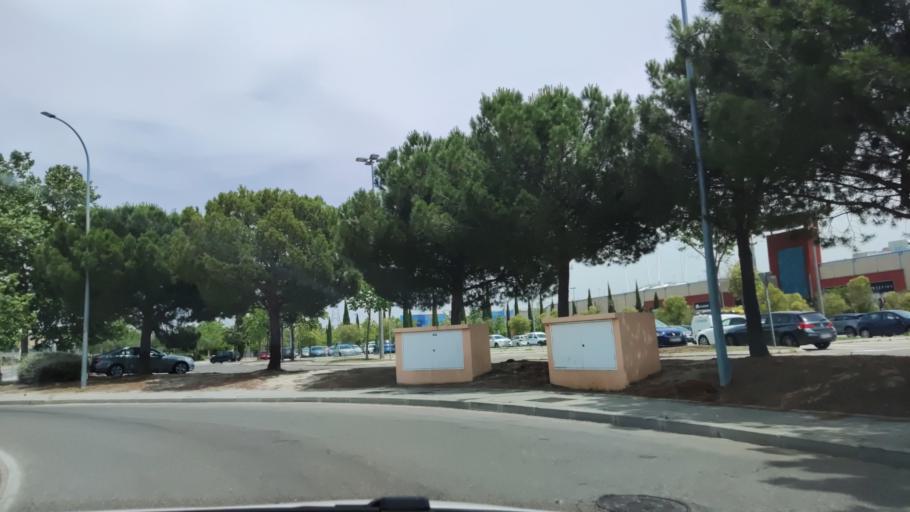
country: ES
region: Madrid
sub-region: Provincia de Madrid
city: Arroyomolinos
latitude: 40.3007
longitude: -3.9282
